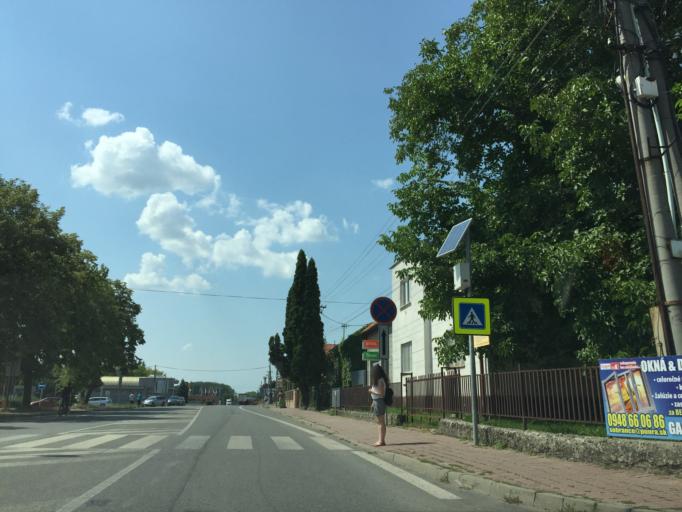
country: SK
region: Kosicky
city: Sobrance
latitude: 48.7465
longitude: 22.1772
